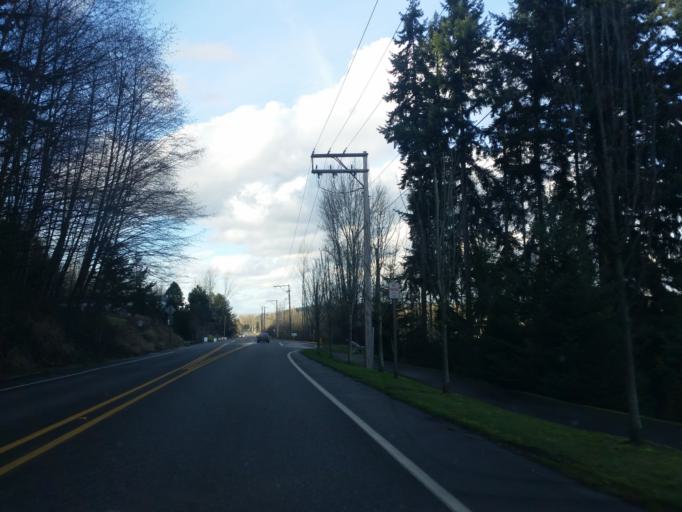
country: US
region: Washington
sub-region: King County
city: Woodinville
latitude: 47.7357
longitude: -122.1543
